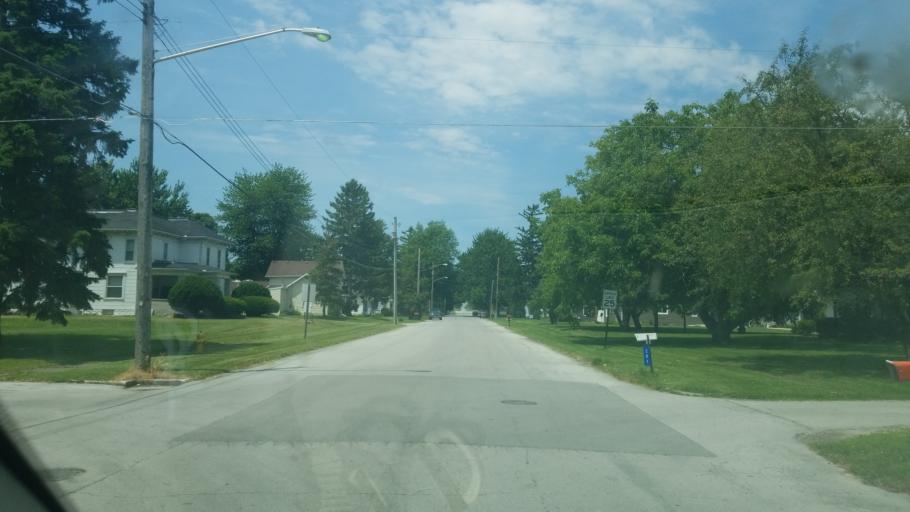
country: US
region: Ohio
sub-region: Wood County
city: North Baltimore
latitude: 41.2538
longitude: -83.6066
